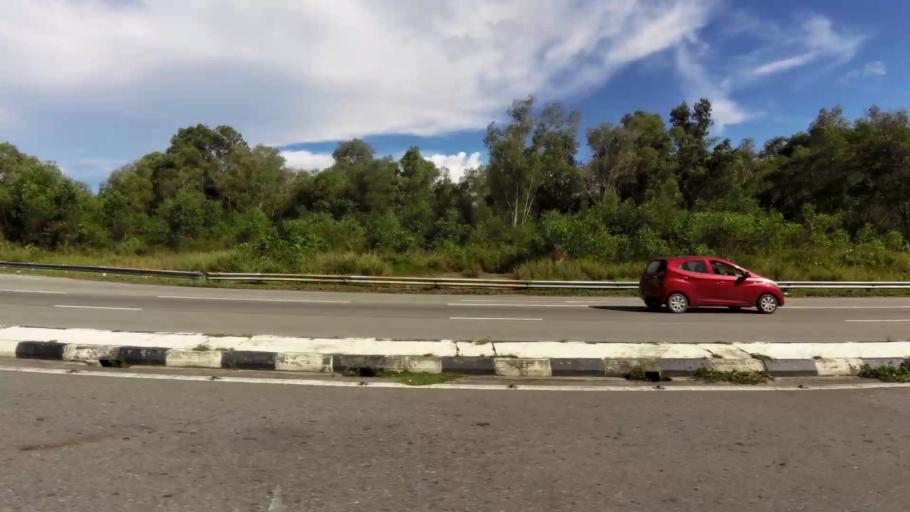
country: BN
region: Brunei and Muara
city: Bandar Seri Begawan
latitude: 4.9841
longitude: 114.9423
